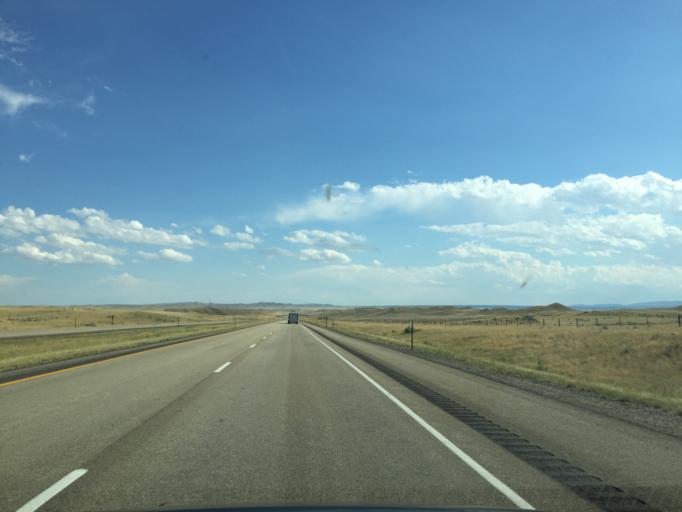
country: US
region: Wyoming
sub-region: Johnson County
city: Buffalo
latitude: 44.1107
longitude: -106.6369
